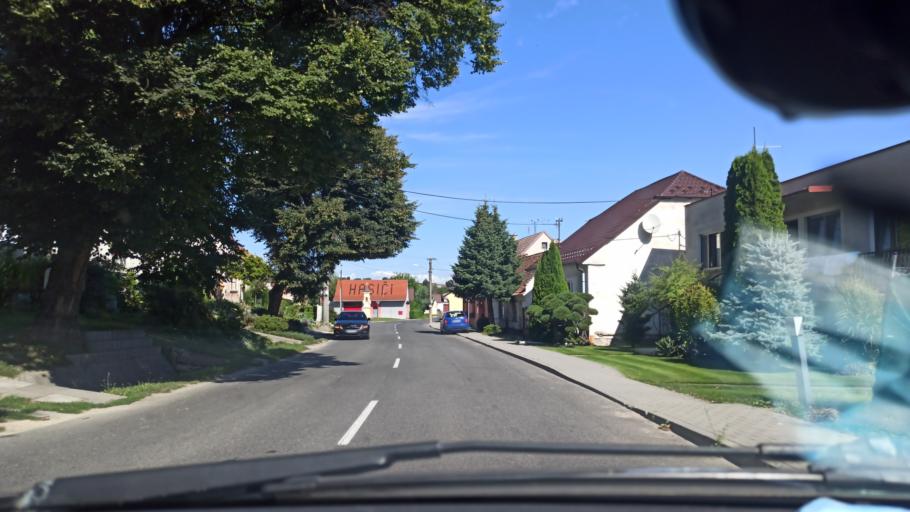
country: SK
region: Trnavsky
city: Gbely
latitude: 48.6756
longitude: 17.2008
